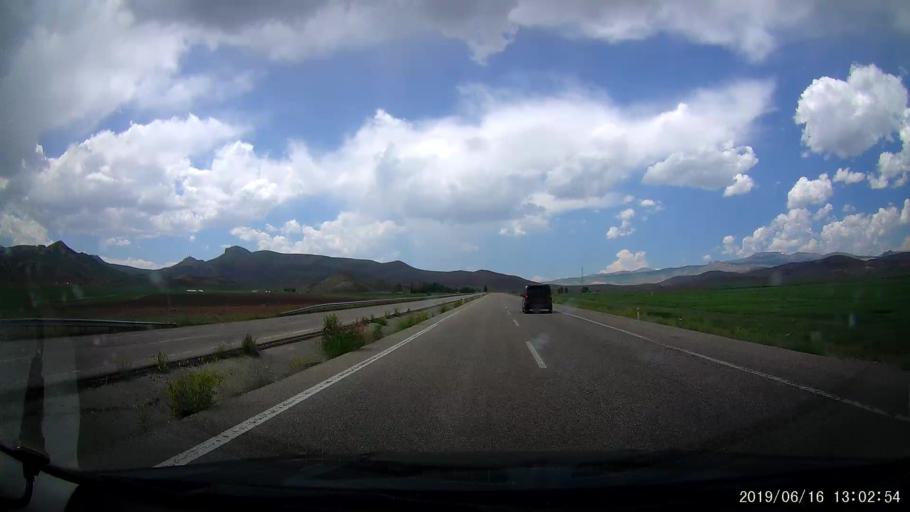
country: TR
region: Agri
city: Sulucem
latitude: 39.5774
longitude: 43.8035
